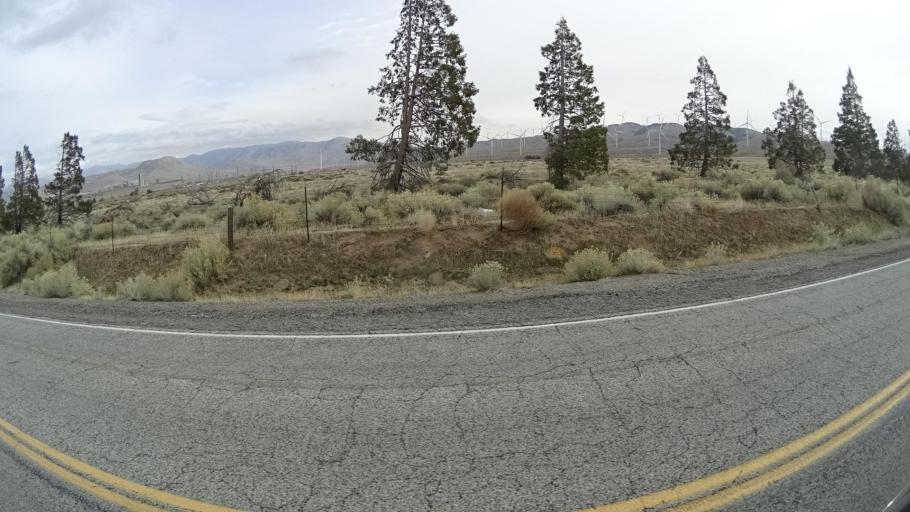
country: US
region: California
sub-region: Kern County
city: Tehachapi
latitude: 35.1016
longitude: -118.3968
